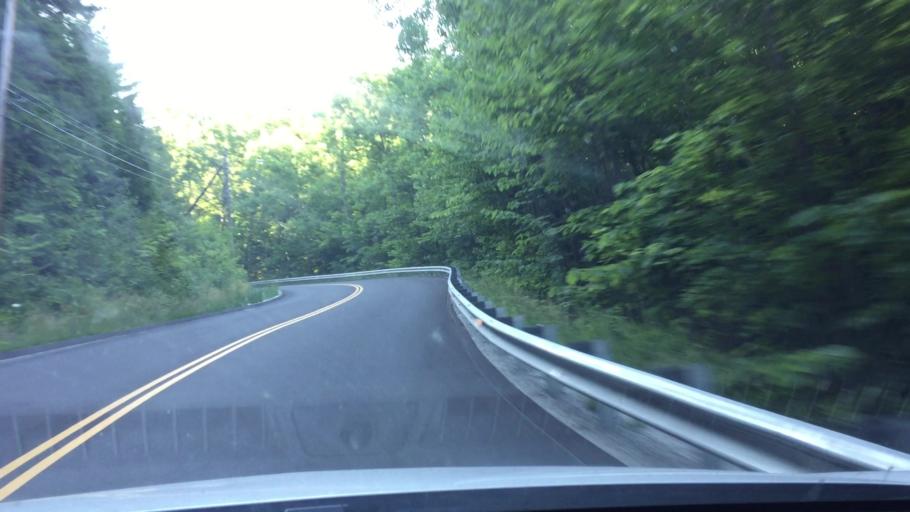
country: US
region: Massachusetts
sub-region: Berkshire County
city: Lee
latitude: 42.2936
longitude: -73.2228
